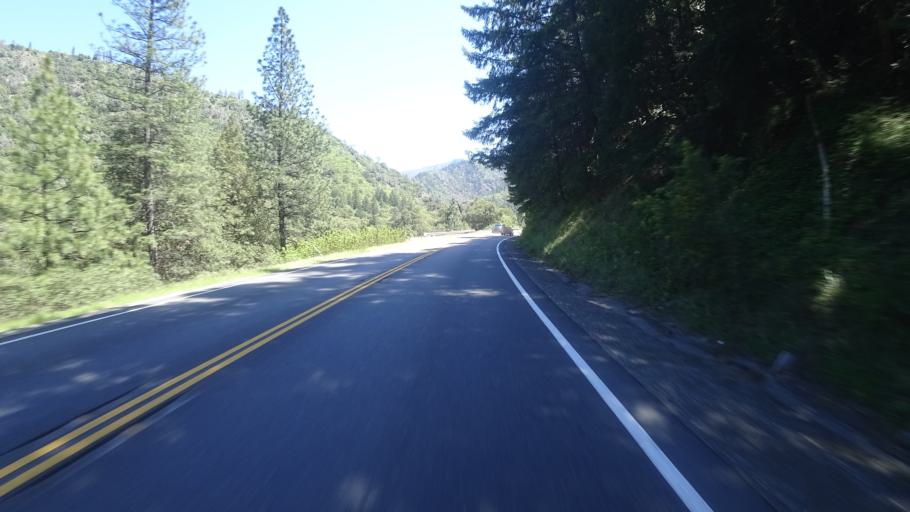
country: US
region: California
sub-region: Humboldt County
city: Willow Creek
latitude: 40.7939
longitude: -123.4575
